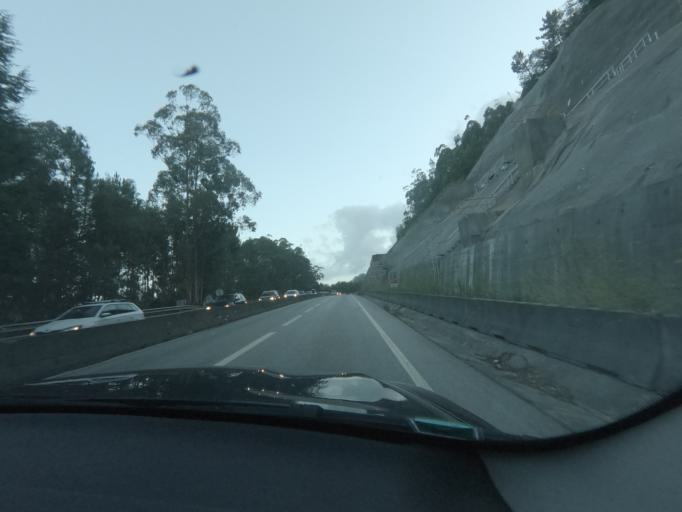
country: PT
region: Coimbra
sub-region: Penacova
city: Penacova
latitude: 40.2781
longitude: -8.2734
